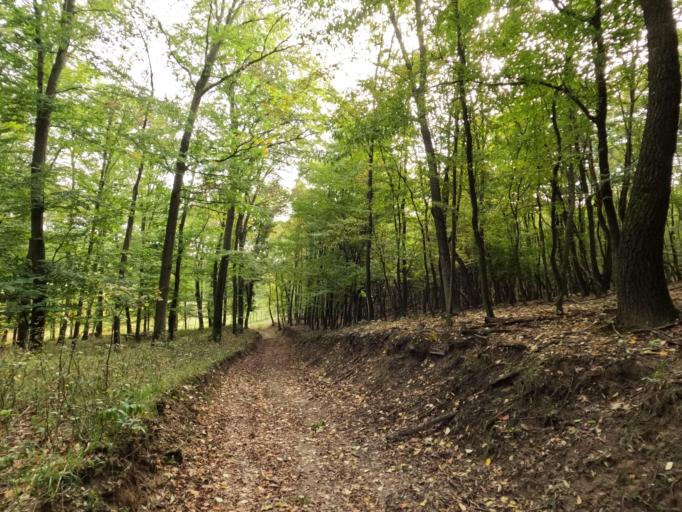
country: HU
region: Tolna
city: Szentgalpuszta
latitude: 46.3130
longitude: 18.6433
